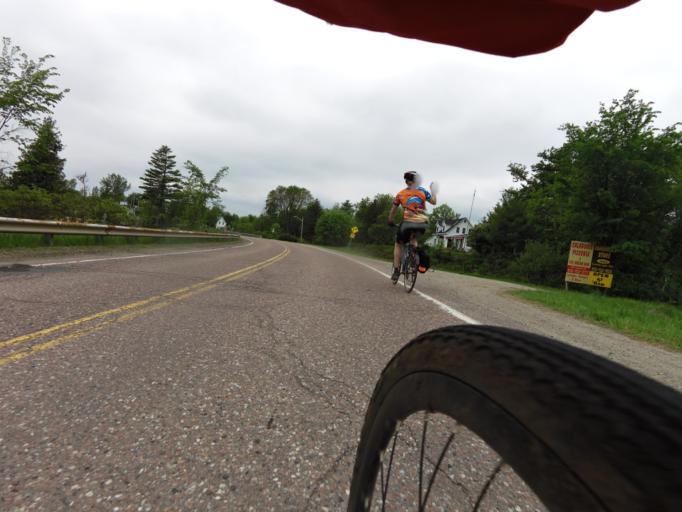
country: CA
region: Ontario
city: Renfrew
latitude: 45.2995
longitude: -76.7185
